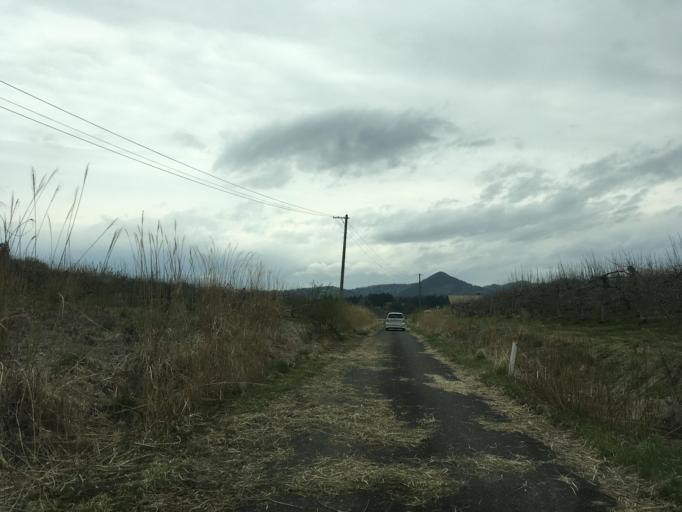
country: JP
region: Iwate
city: Ichinoseki
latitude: 38.8495
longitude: 141.3304
